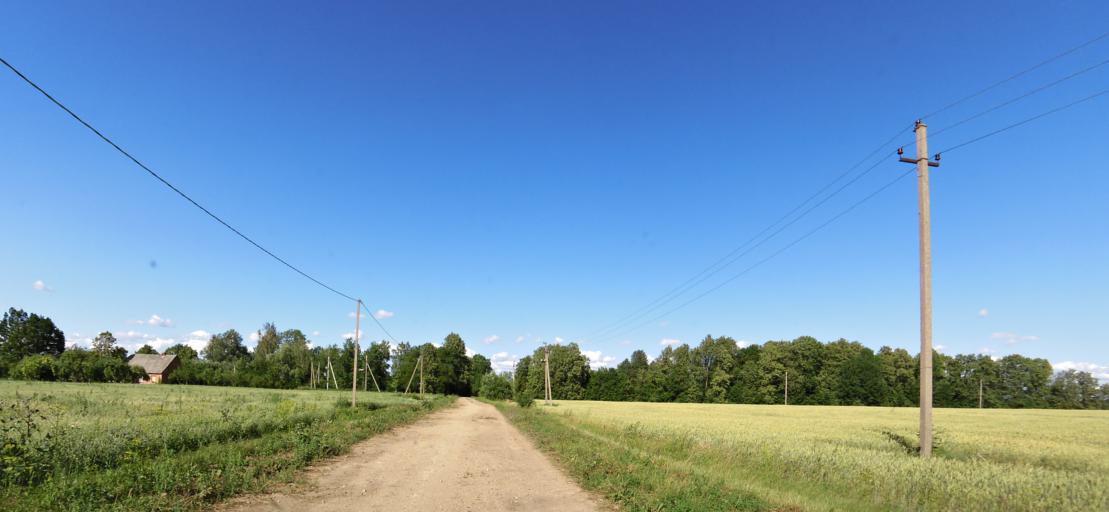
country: LT
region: Panevezys
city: Pasvalys
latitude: 56.1696
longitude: 24.4278
